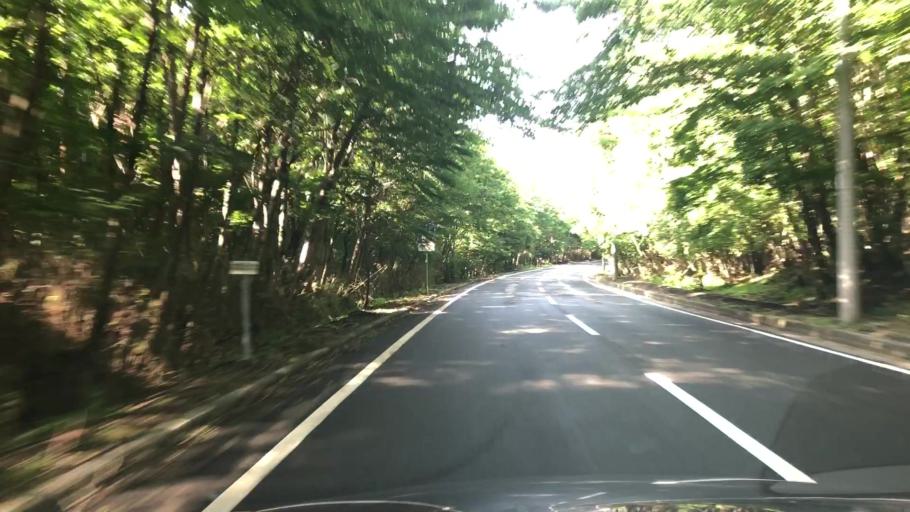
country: JP
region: Shizuoka
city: Gotemba
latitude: 35.3160
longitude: 138.7871
